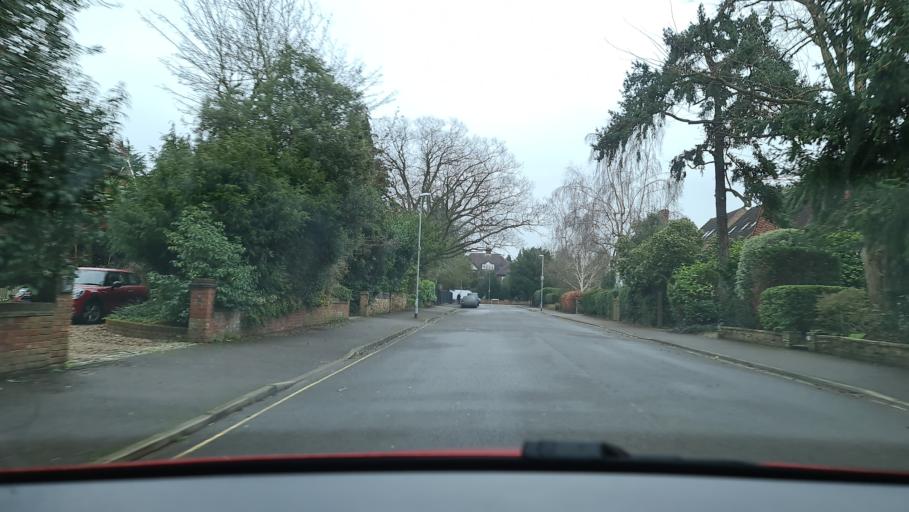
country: GB
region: England
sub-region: Greater London
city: Surbiton
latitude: 51.3863
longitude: -0.3041
